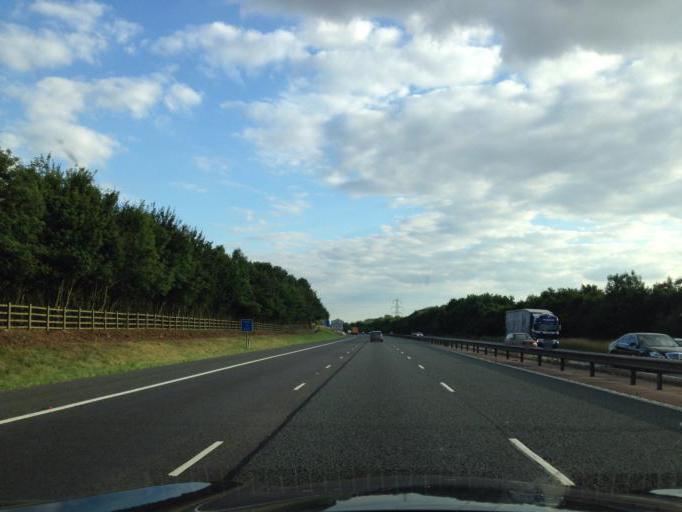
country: GB
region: England
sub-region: Oxfordshire
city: Wheatley
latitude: 51.7625
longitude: -1.1046
